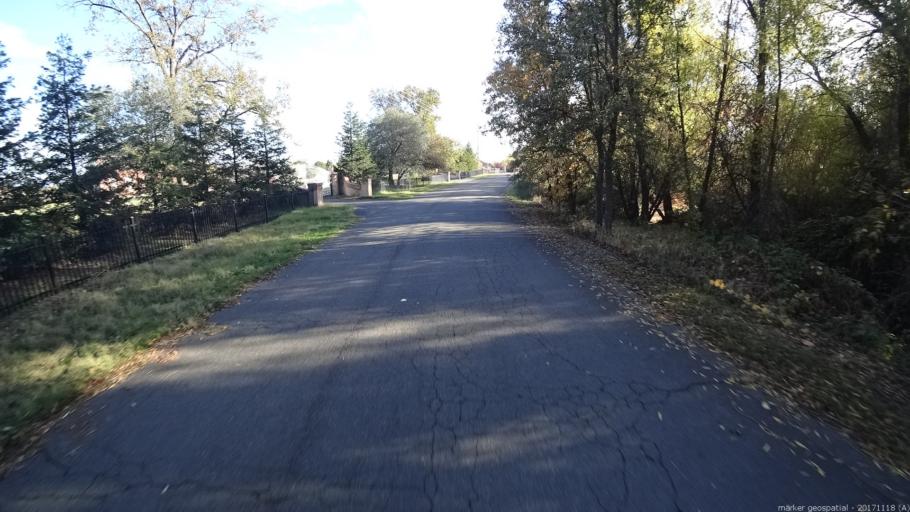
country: US
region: California
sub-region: Shasta County
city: Cottonwood
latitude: 40.3764
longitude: -122.3388
